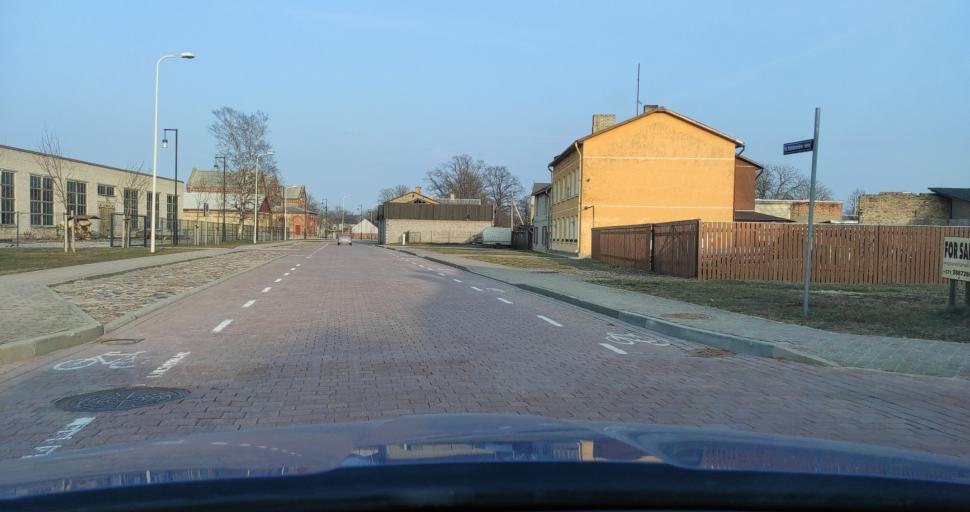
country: LV
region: Ventspils
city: Ventspils
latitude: 57.3937
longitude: 21.5437
